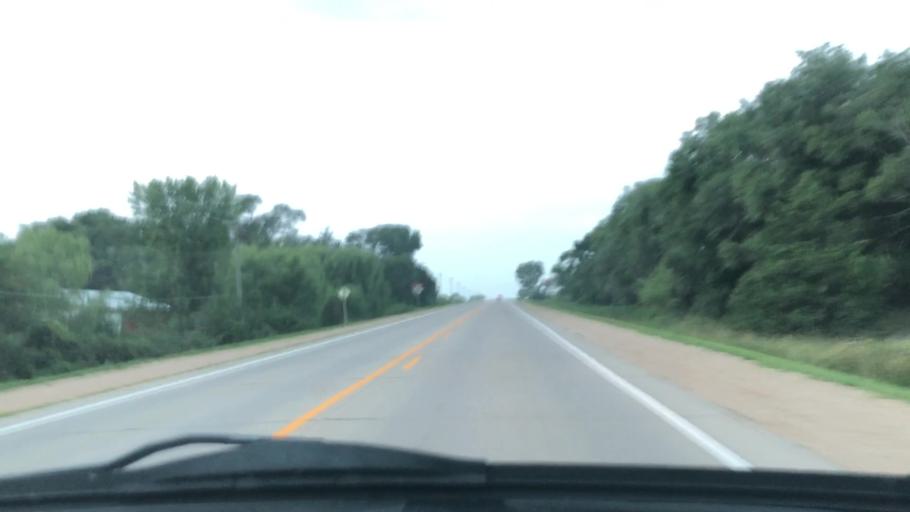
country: US
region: Iowa
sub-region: Linn County
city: Ely
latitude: 41.8493
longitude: -91.6754
